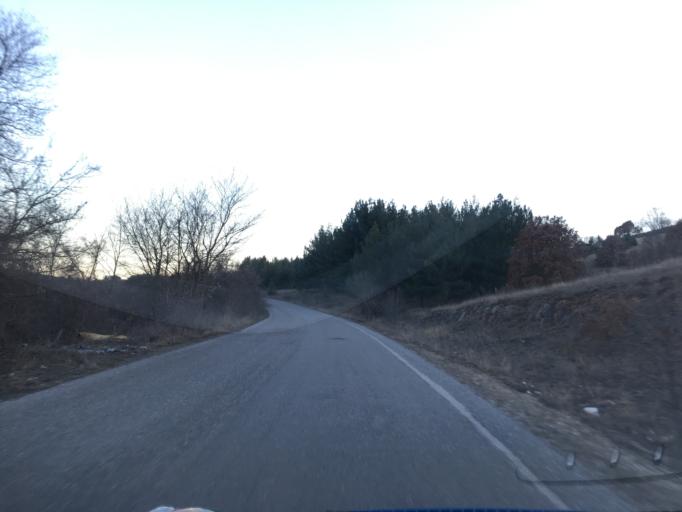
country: GR
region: West Macedonia
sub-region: Nomos Kozanis
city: Koila
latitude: 40.3259
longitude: 21.8129
